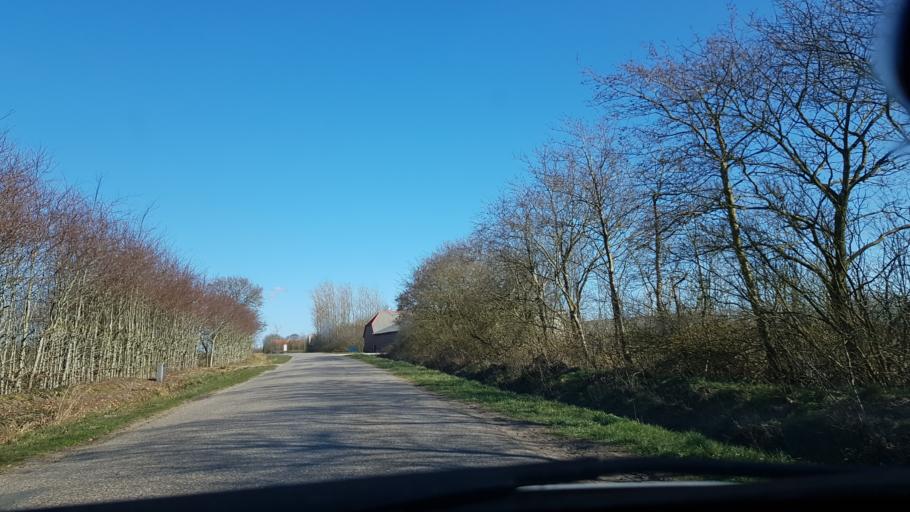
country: DK
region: South Denmark
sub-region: Tonder Kommune
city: Sherrebek
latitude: 55.2275
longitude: 8.7613
